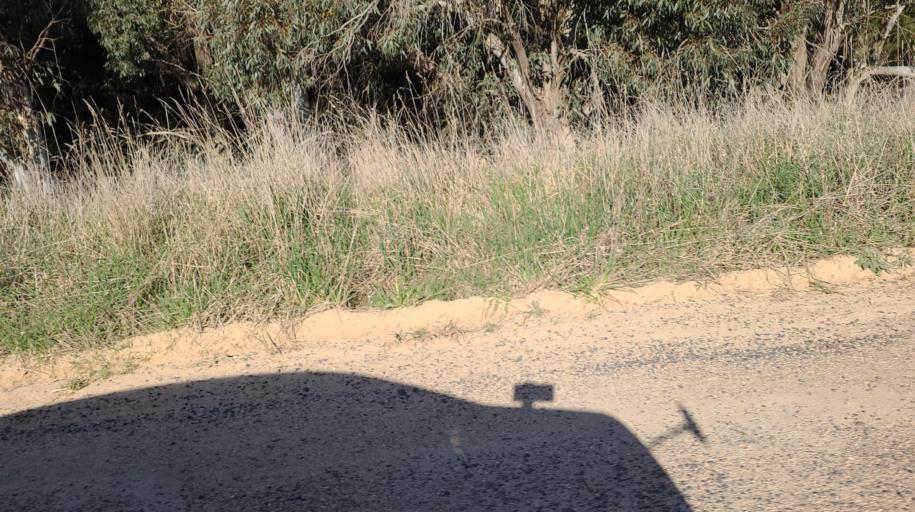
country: AU
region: New South Wales
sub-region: Blayney
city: Millthorpe
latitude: -33.4107
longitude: 149.3064
